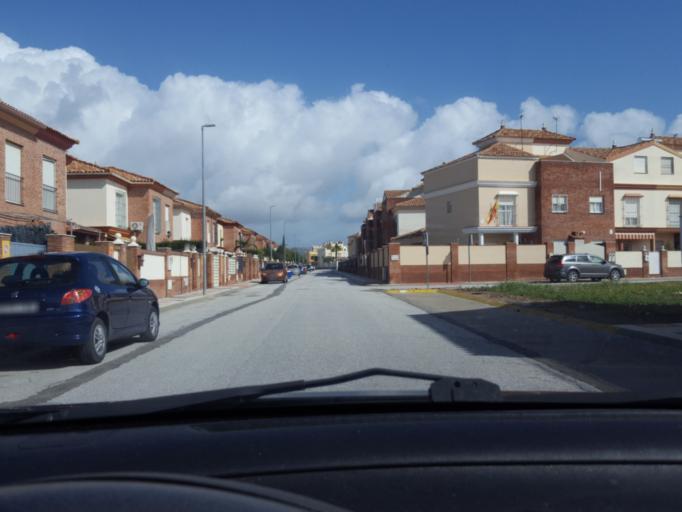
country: ES
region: Andalusia
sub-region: Provincia de Sevilla
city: Acala del Rio
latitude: 37.5178
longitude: -5.9870
